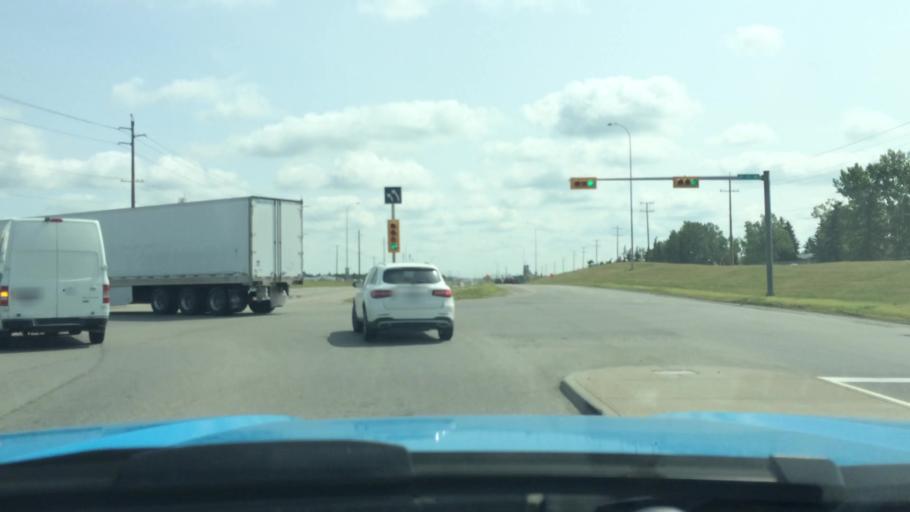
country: CA
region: Alberta
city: Calgary
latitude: 51.0960
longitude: -113.9664
